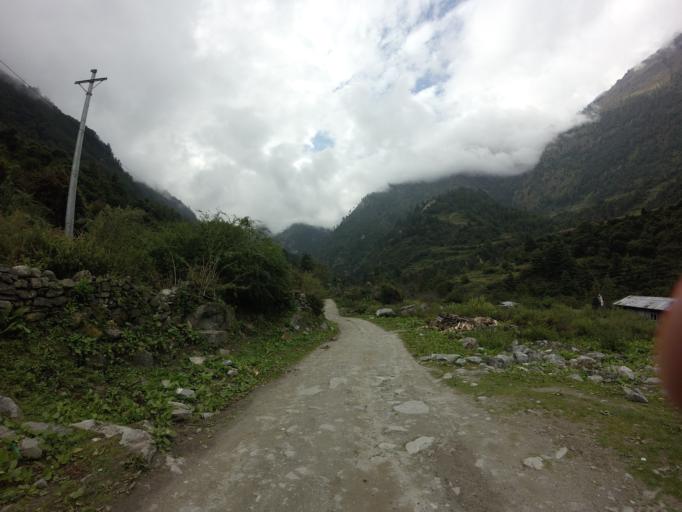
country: NP
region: Western Region
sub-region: Gandaki Zone
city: Chame
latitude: 28.5334
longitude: 84.3382
